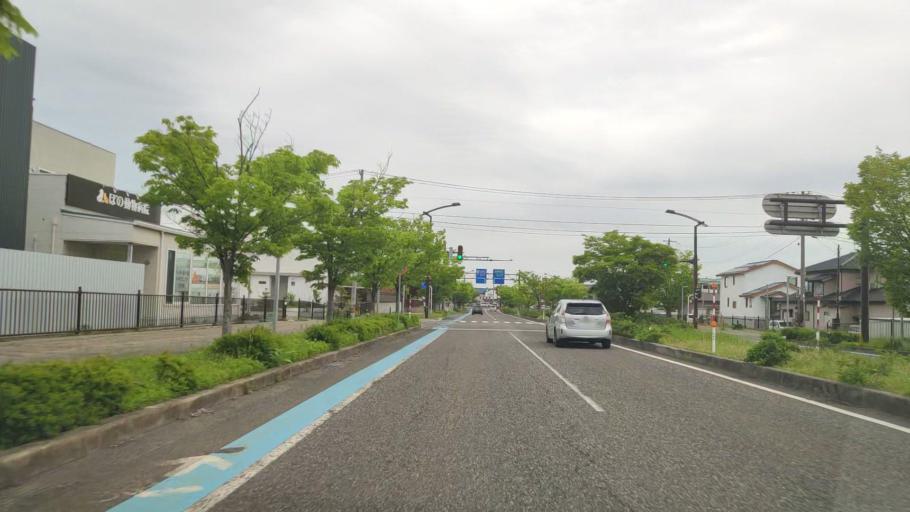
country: JP
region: Niigata
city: Kameda-honcho
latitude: 37.8846
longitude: 139.0706
